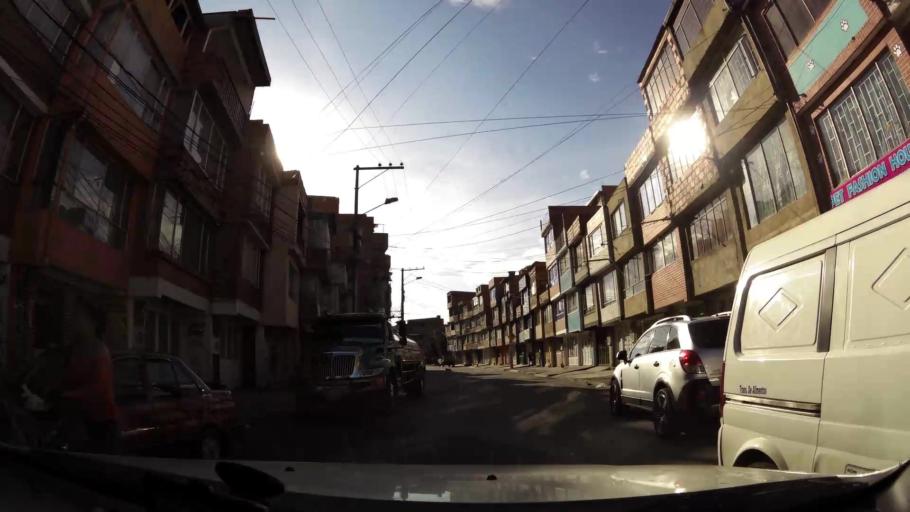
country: CO
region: Cundinamarca
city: Soacha
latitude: 4.5735
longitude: -74.1508
